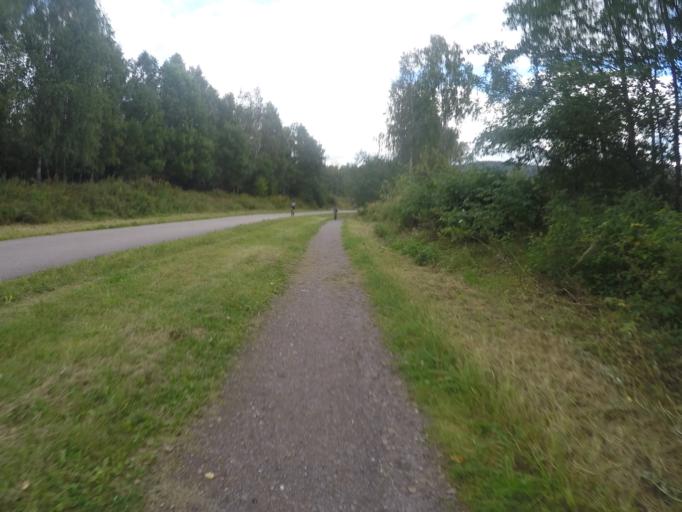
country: NO
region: Oslo
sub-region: Oslo
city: Oslo
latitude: 59.9695
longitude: 10.7702
